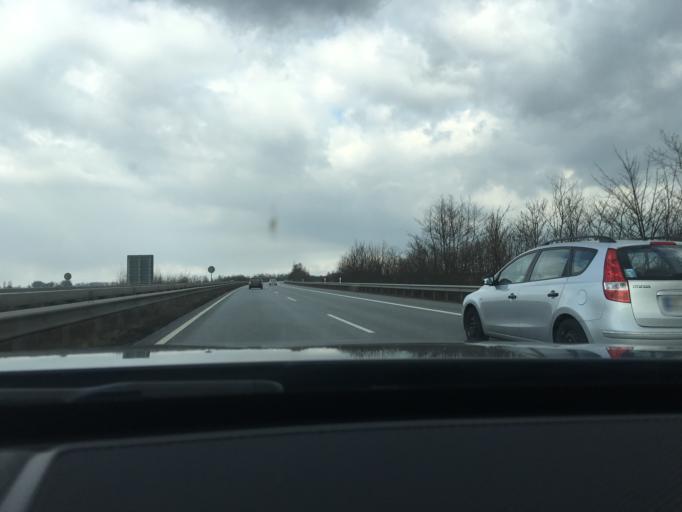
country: DE
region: Lower Saxony
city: Driftsethe
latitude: 53.3786
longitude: 8.5747
